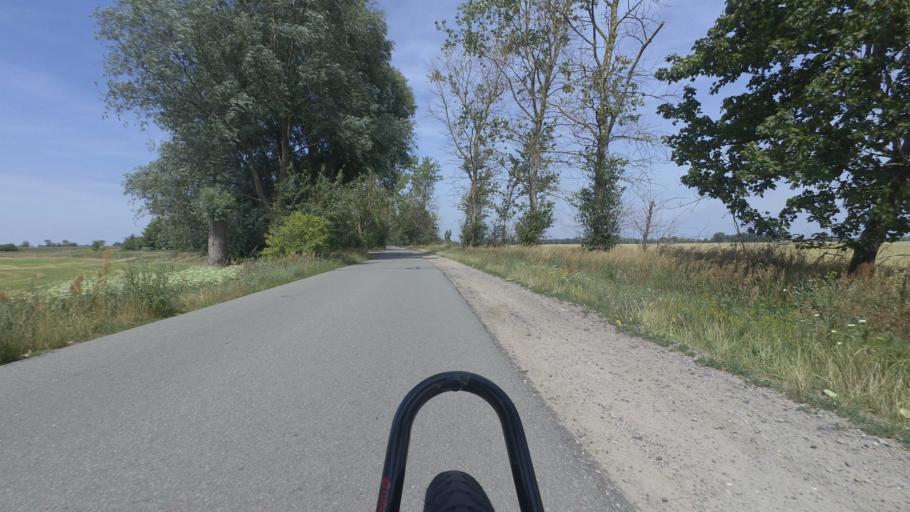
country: DE
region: Brandenburg
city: Rhinow
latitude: 52.7594
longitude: 12.3317
